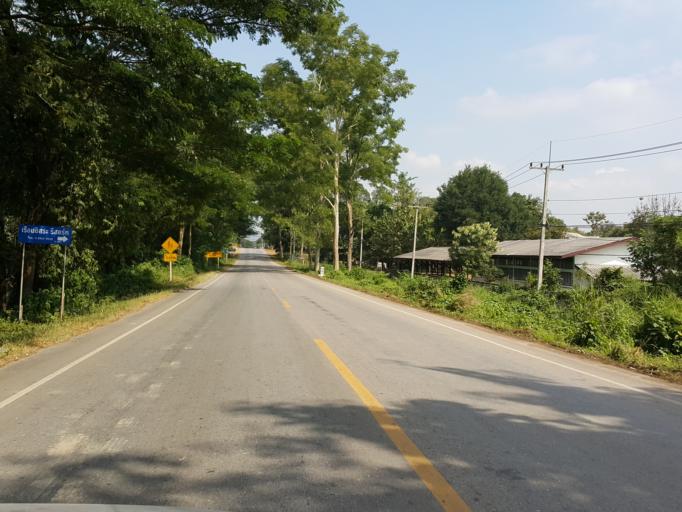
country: TH
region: Sukhothai
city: Thung Saliam
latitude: 17.3379
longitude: 99.5897
